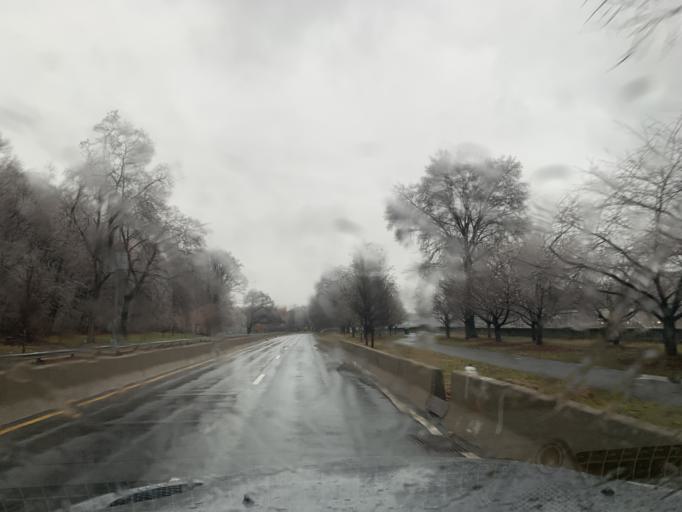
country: US
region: New York
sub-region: New York County
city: Inwood
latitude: 40.8532
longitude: -73.9246
